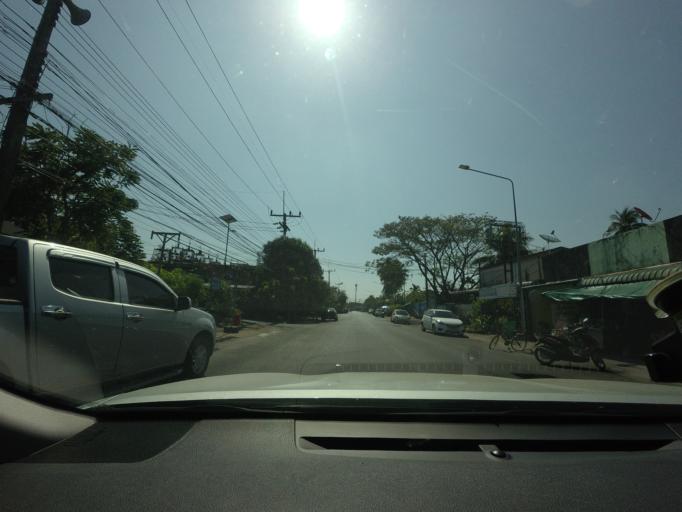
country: TH
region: Yala
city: Yala
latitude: 6.5446
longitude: 101.2857
